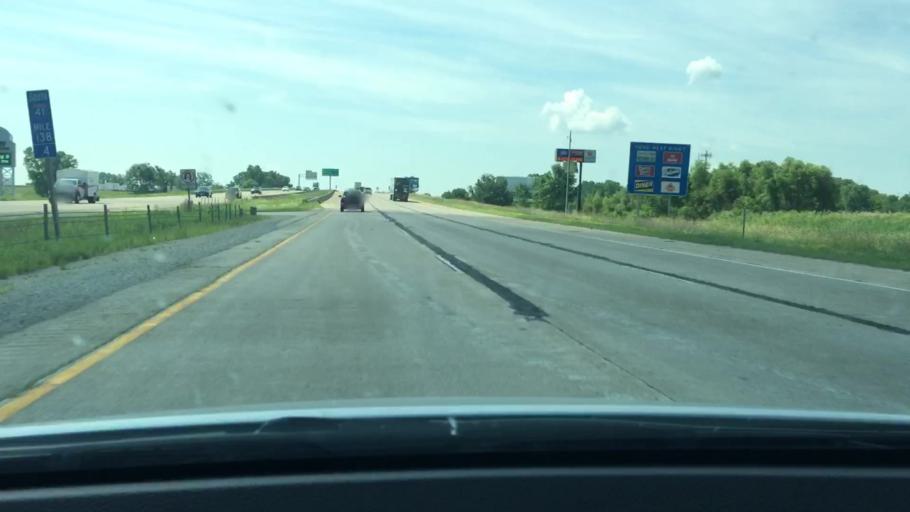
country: US
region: Wisconsin
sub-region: Outagamie County
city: Appleton
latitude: 44.2836
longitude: -88.4664
